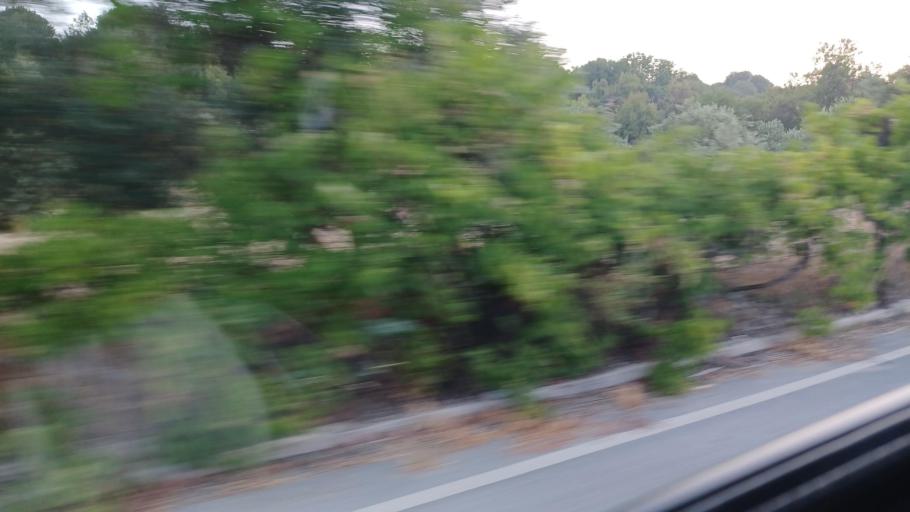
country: CY
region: Pafos
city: Mesogi
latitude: 34.8307
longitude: 32.5717
